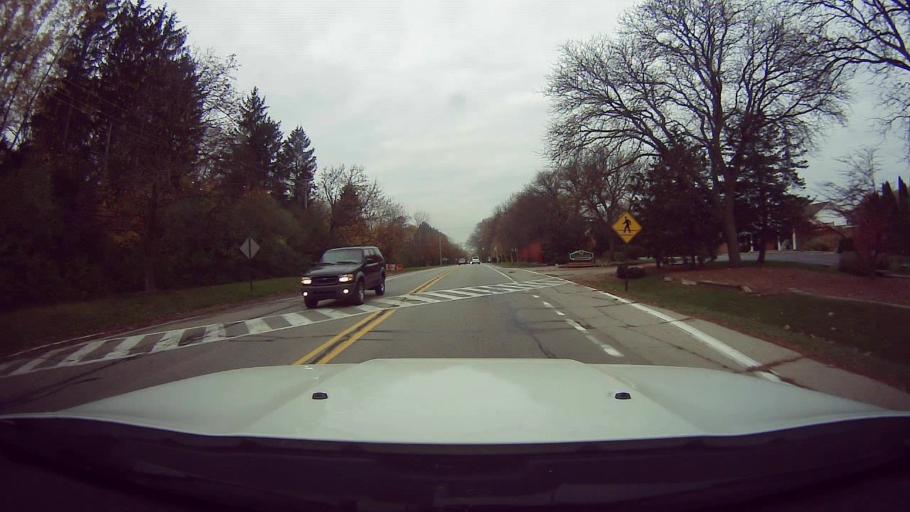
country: US
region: Michigan
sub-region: Oakland County
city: Bingham Farms
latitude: 42.5160
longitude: -83.2671
